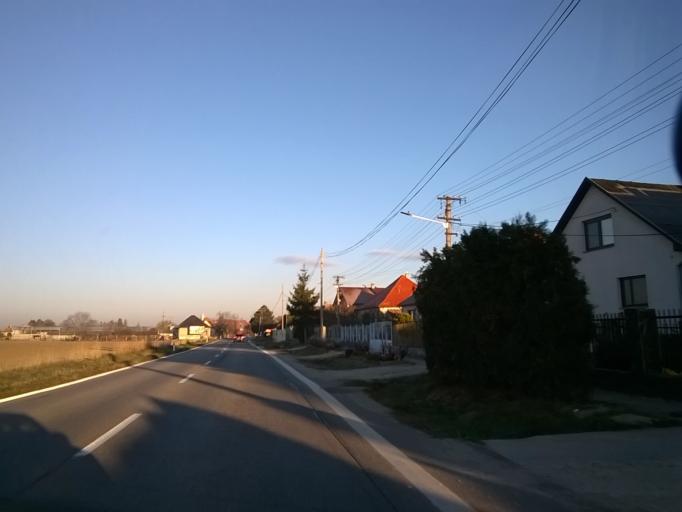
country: SK
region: Nitriansky
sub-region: Okres Nitra
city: Nitra
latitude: 48.3465
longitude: 18.0621
